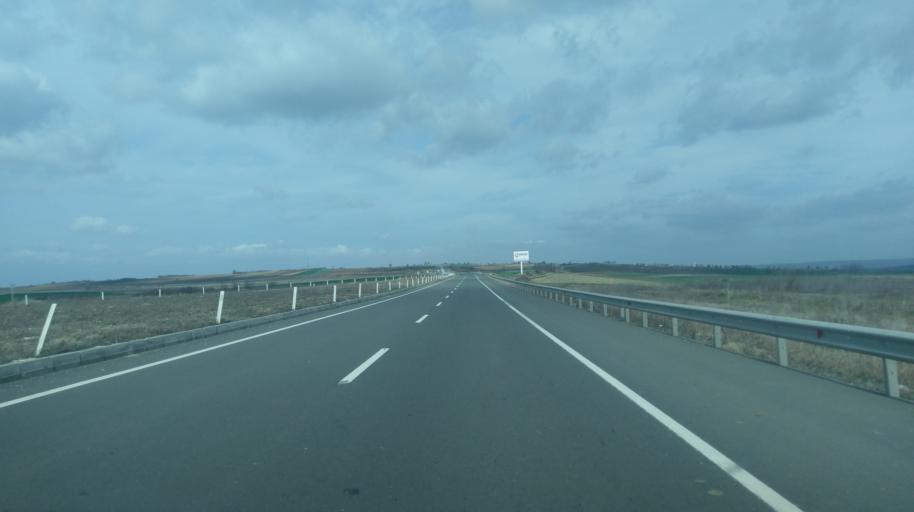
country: TR
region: Edirne
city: Hamidiye
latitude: 41.0420
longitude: 26.6346
